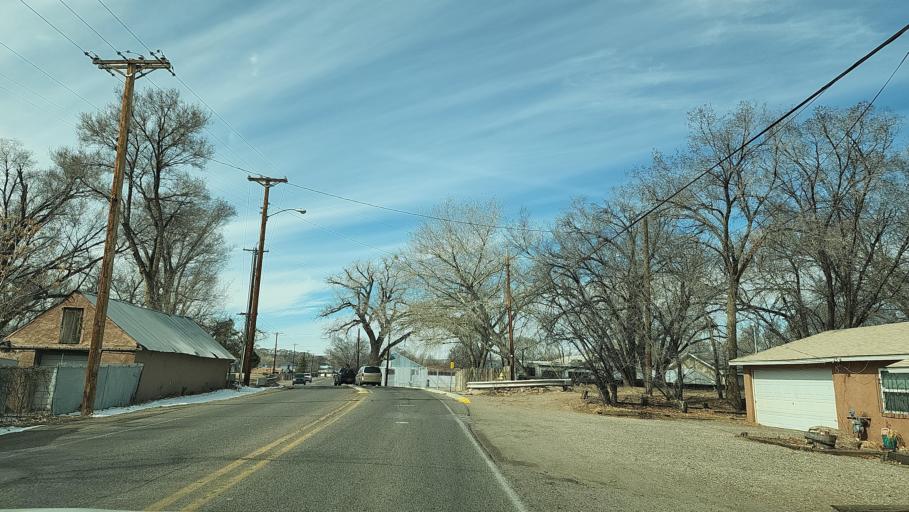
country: US
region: New Mexico
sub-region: Bernalillo County
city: South Valley
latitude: 35.0364
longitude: -106.6978
